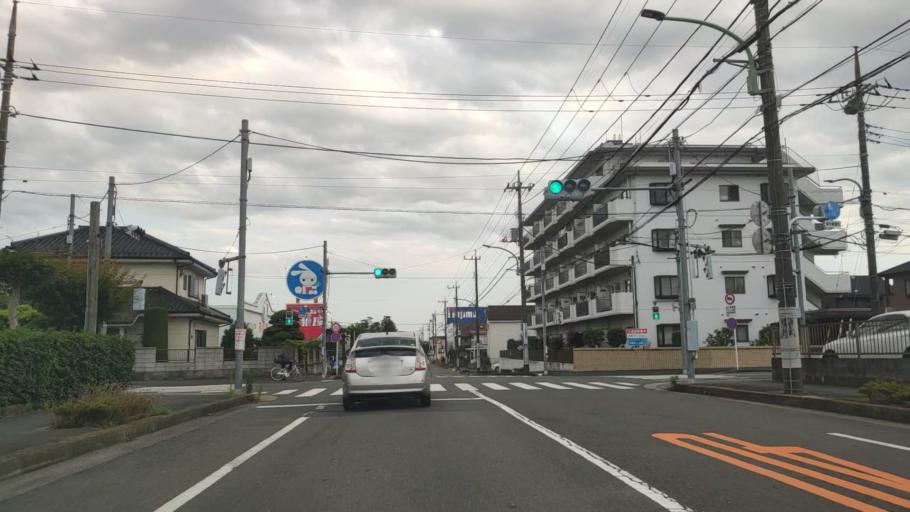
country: JP
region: Tokyo
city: Ome
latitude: 35.7933
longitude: 139.2986
